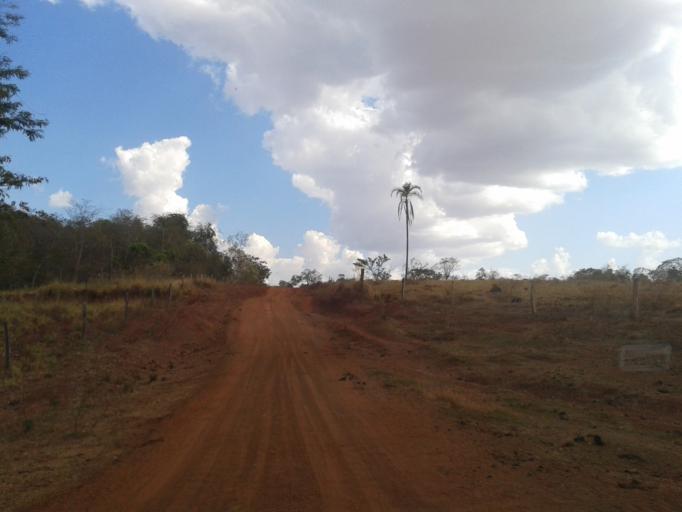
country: BR
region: Minas Gerais
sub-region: Santa Vitoria
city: Santa Vitoria
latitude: -19.2479
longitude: -49.9782
